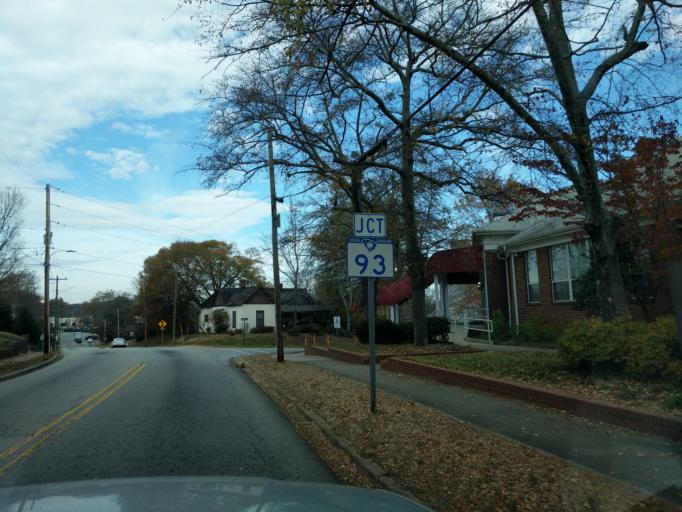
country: US
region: South Carolina
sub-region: Pickens County
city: Easley
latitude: 34.8262
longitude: -82.6101
